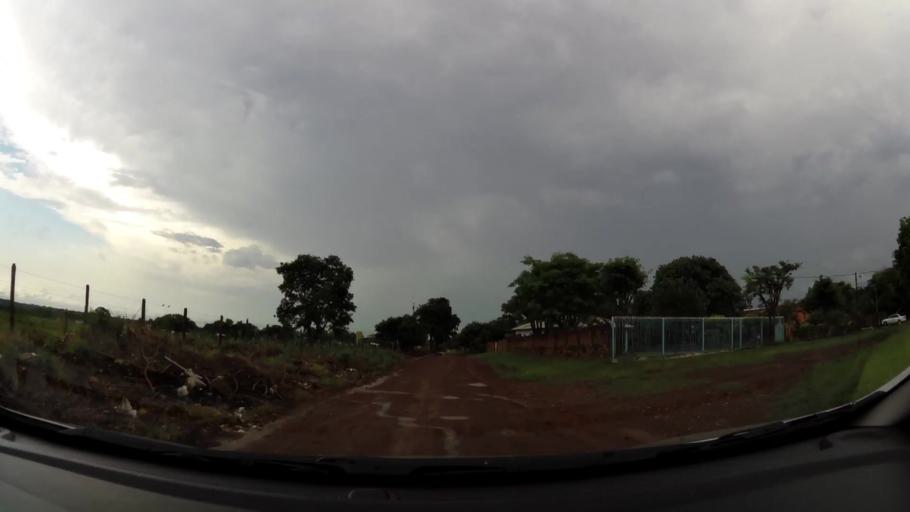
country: PY
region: Alto Parana
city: Presidente Franco
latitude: -25.5460
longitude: -54.6491
